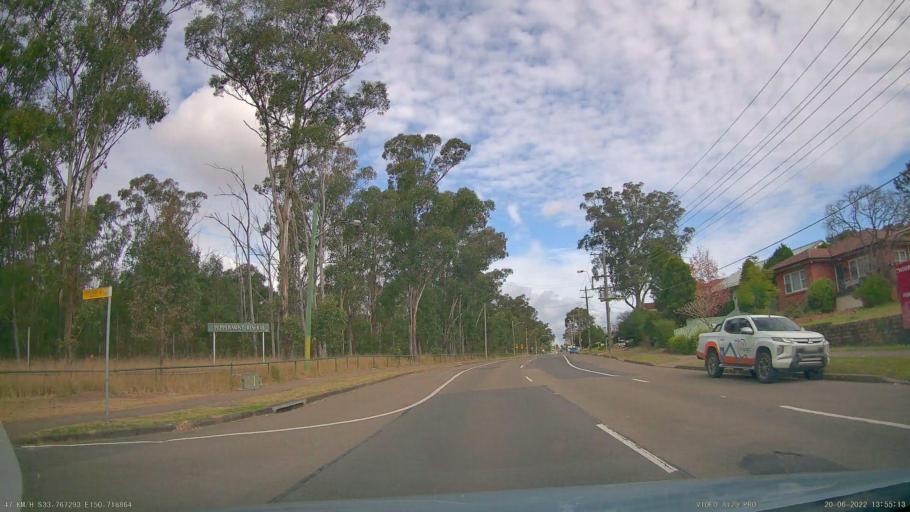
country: AU
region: New South Wales
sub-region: Penrith Municipality
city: Kingswood Park
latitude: -33.7674
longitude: 150.7189
